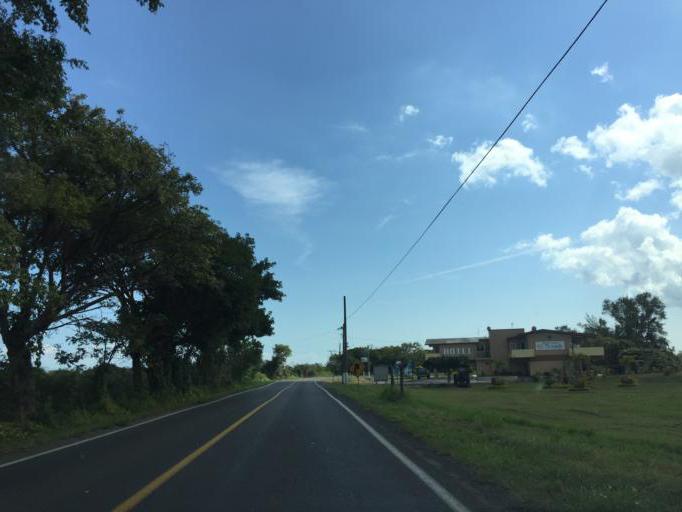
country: MX
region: Veracruz
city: Gutierrez Zamora
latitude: 20.4813
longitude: -97.0653
